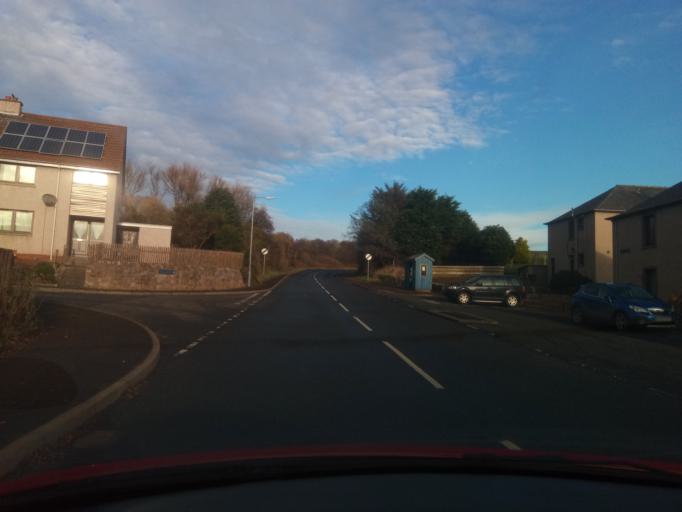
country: GB
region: Scotland
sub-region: The Scottish Borders
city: Eyemouth
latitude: 55.8893
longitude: -2.1507
